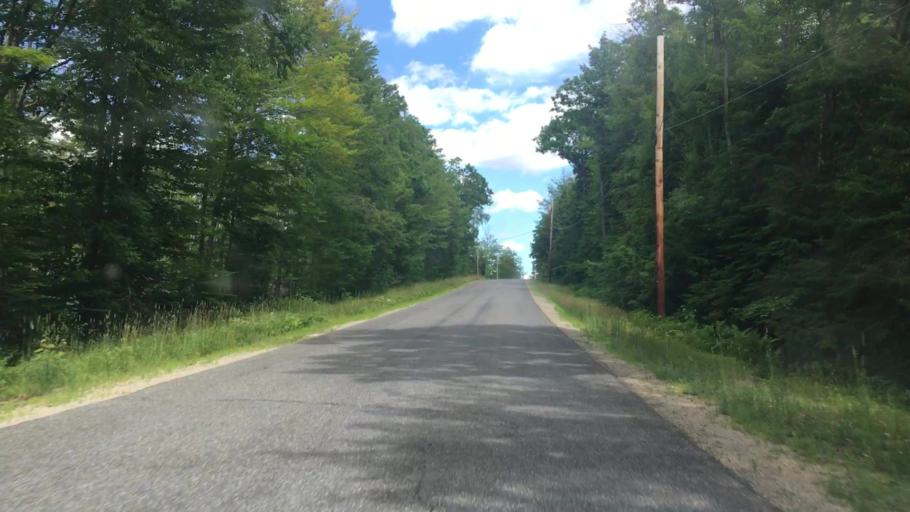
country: US
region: Maine
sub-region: Franklin County
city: Jay
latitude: 44.5365
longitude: -70.1982
